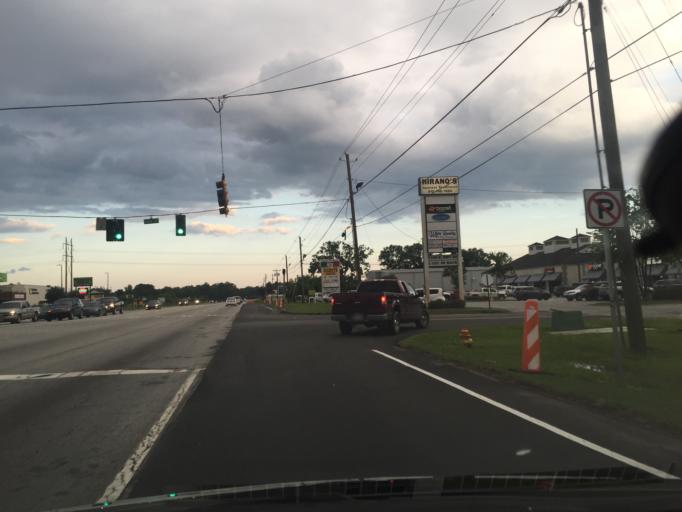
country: US
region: Georgia
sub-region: Chatham County
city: Pooler
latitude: 32.1069
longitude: -81.2290
